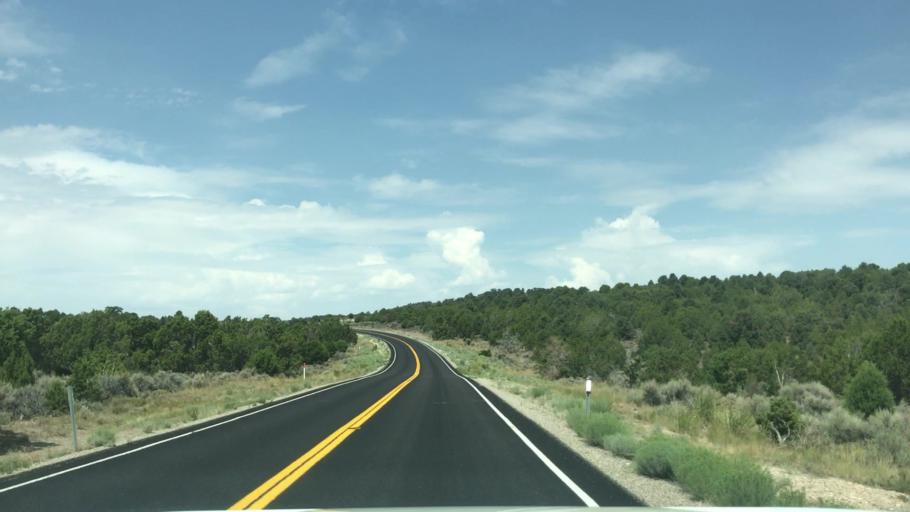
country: US
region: Nevada
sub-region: Eureka County
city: Eureka
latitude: 39.3954
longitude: -115.4624
